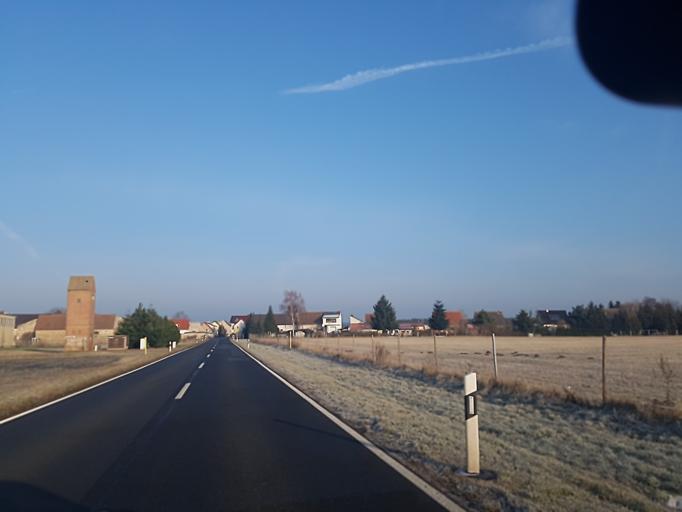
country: DE
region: Brandenburg
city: Golzow
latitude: 52.2442
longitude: 12.6959
